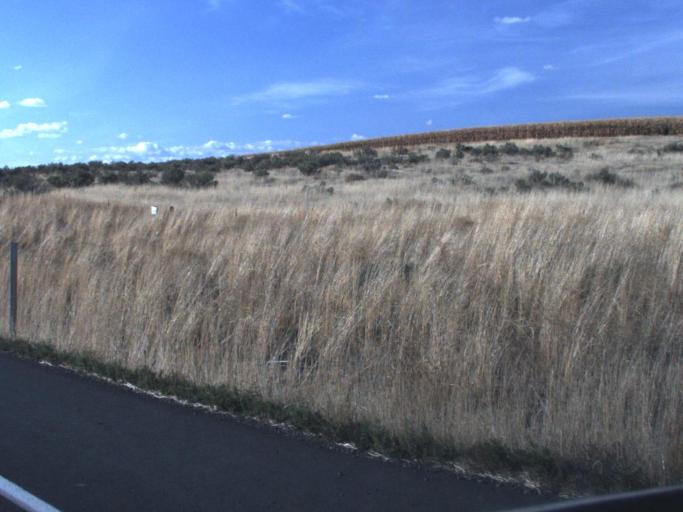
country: US
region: Oregon
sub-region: Umatilla County
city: Umatilla
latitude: 45.9490
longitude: -119.3984
